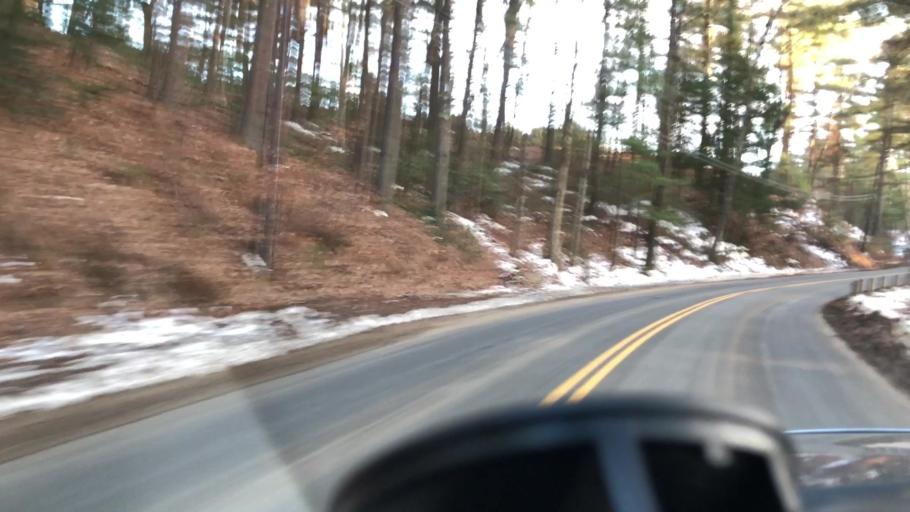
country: US
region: Massachusetts
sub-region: Hampshire County
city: Southampton
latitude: 42.2094
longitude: -72.6793
